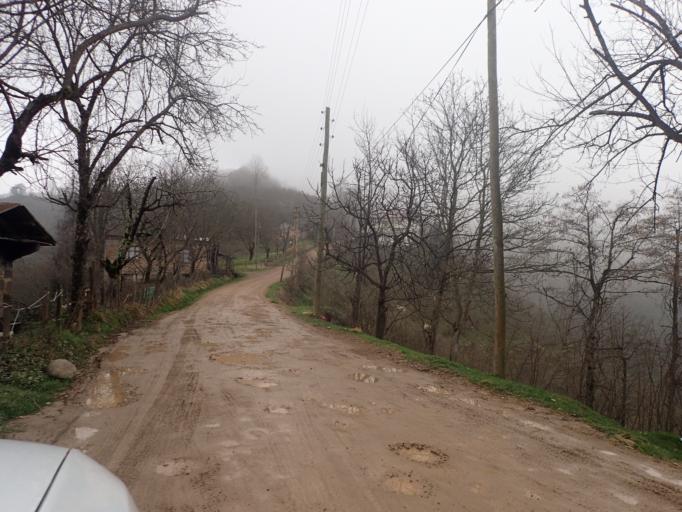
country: TR
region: Ordu
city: Camas
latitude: 40.9097
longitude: 37.5664
